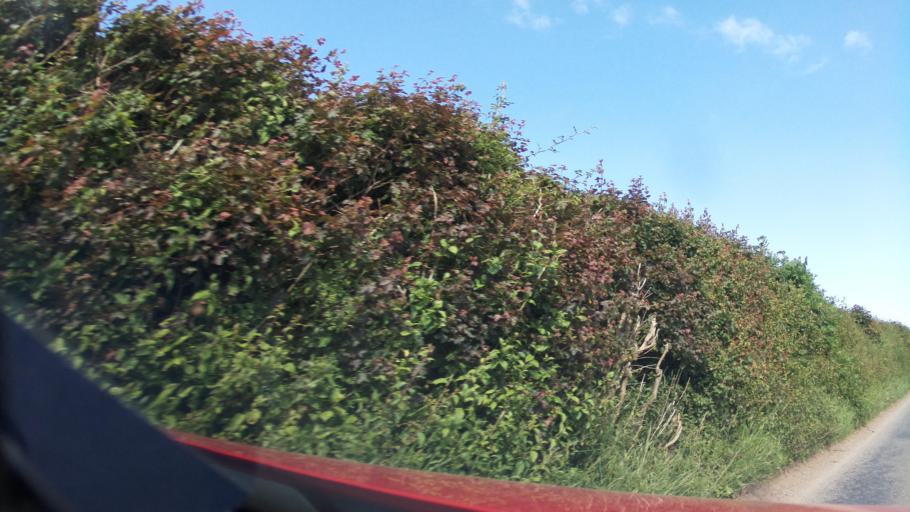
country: GB
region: England
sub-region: Devon
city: Totnes
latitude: 50.4415
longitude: -3.6421
